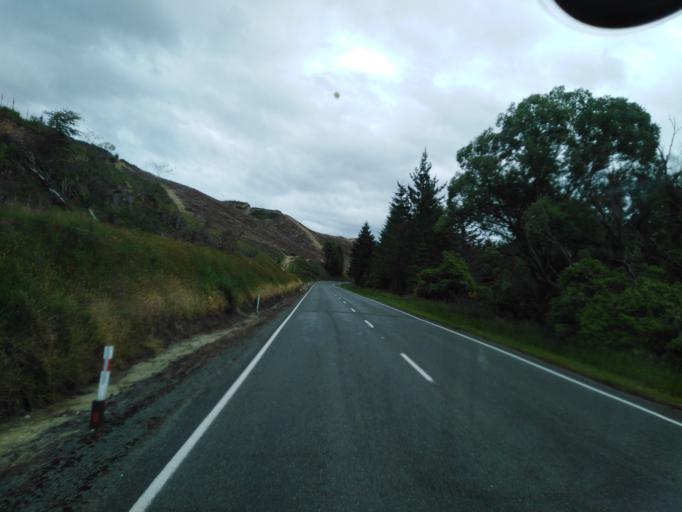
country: NZ
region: Tasman
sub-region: Tasman District
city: Wakefield
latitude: -41.5936
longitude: 172.7637
